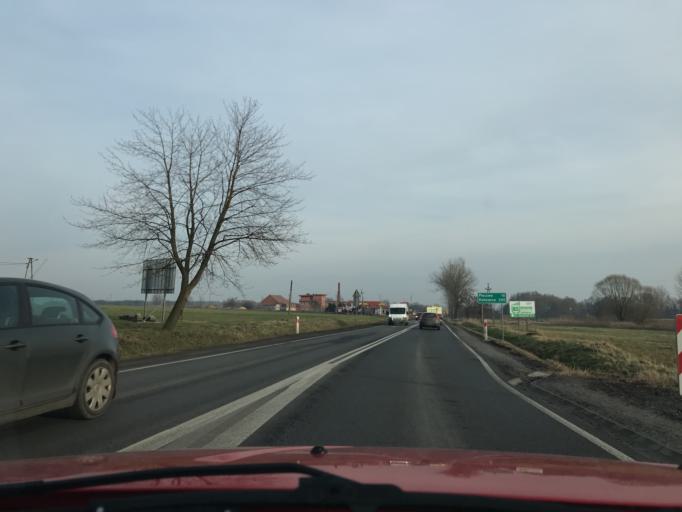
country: PL
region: Greater Poland Voivodeship
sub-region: Powiat jarocinski
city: Witaszyce
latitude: 51.9427
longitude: 17.5727
